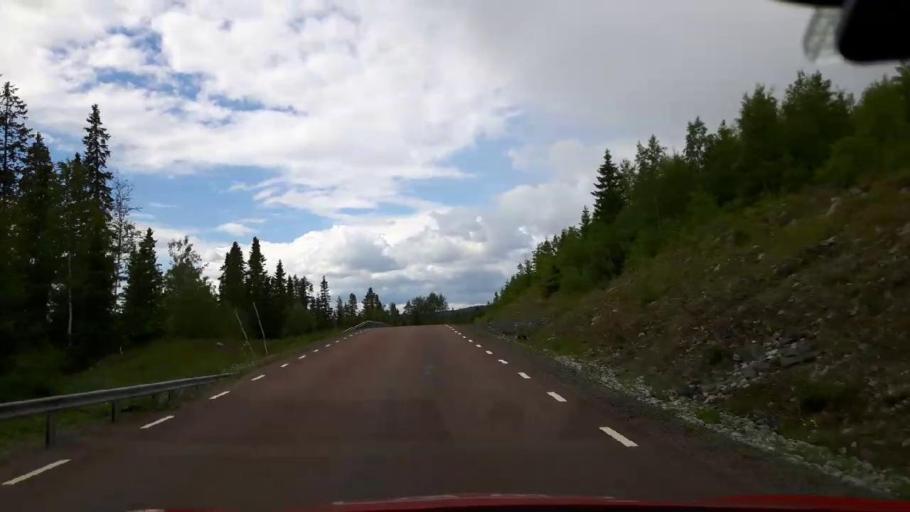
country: SE
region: Jaemtland
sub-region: Krokoms Kommun
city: Valla
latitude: 64.0875
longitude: 14.0610
